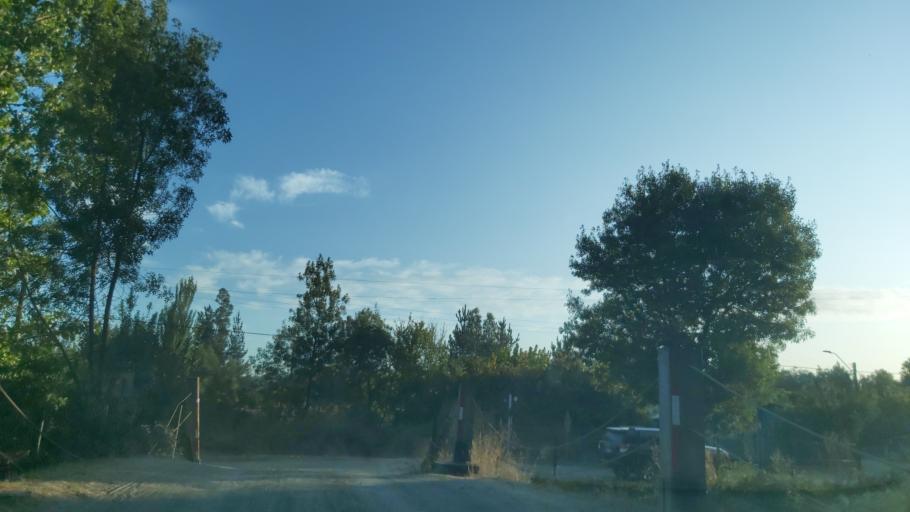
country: CL
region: Biobio
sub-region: Provincia de Biobio
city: La Laja
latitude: -37.1620
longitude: -72.9121
